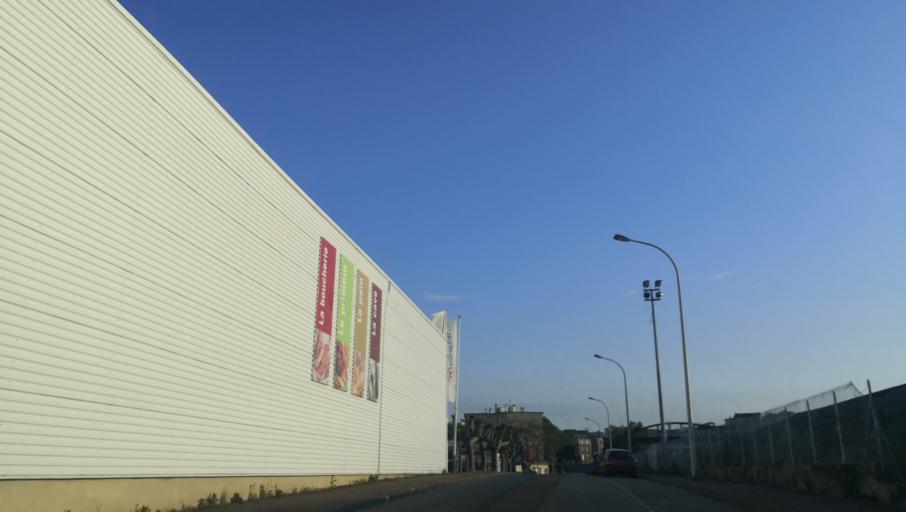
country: FR
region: Limousin
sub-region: Departement de la Haute-Vienne
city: Limoges
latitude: 45.8402
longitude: 1.2534
